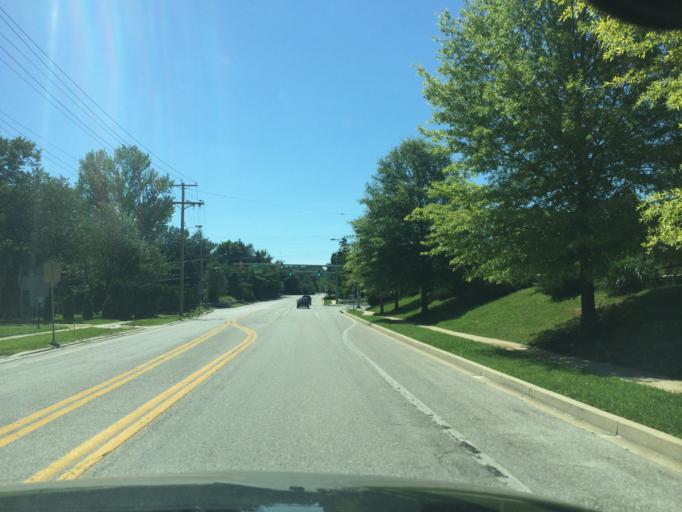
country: US
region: Maryland
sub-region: Baltimore County
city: Mays Chapel
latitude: 39.4247
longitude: -76.6475
